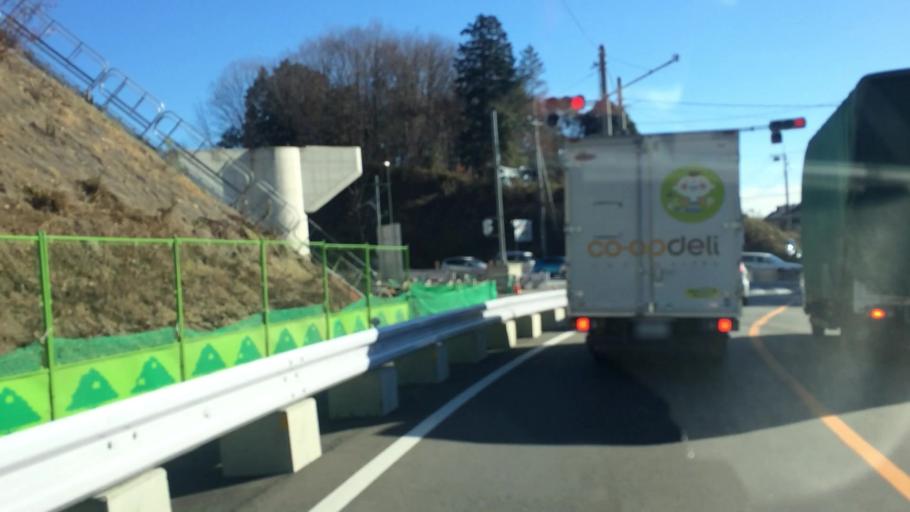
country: JP
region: Tochigi
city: Utsunomiya-shi
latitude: 36.5934
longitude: 139.8680
